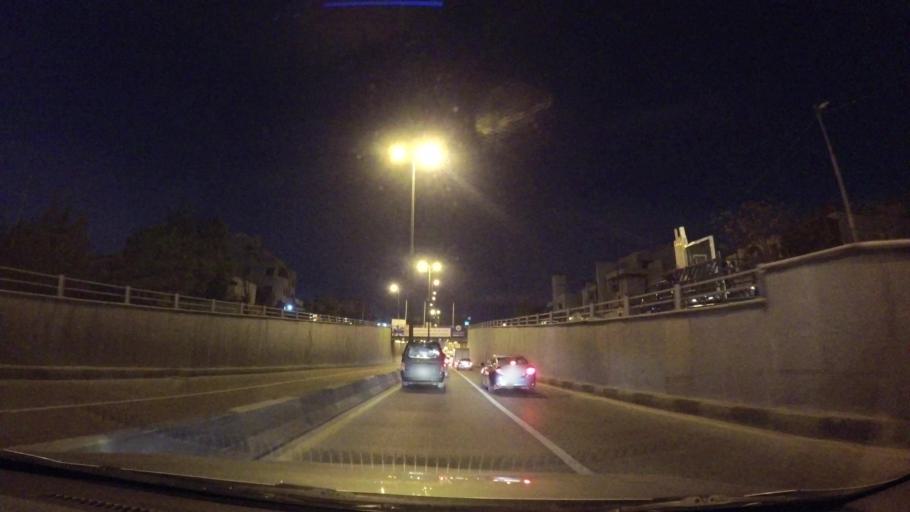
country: JO
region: Amman
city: Al Bunayyat ash Shamaliyah
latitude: 31.9447
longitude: 35.8906
